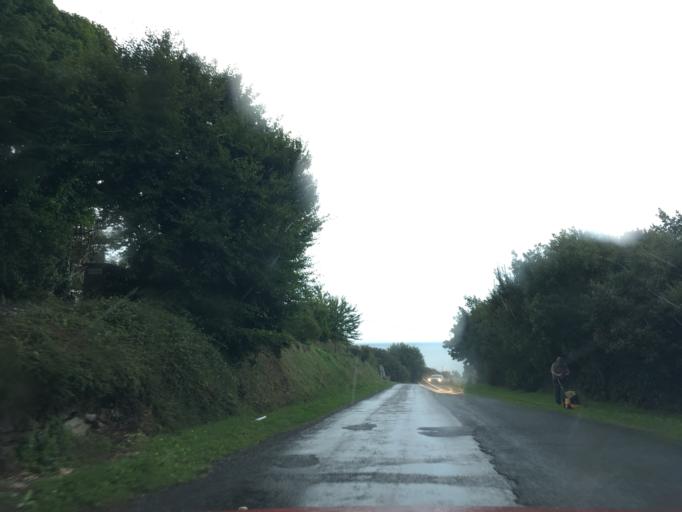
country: IE
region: Munster
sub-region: County Cork
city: Crosshaven
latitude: 51.7842
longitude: -8.3035
